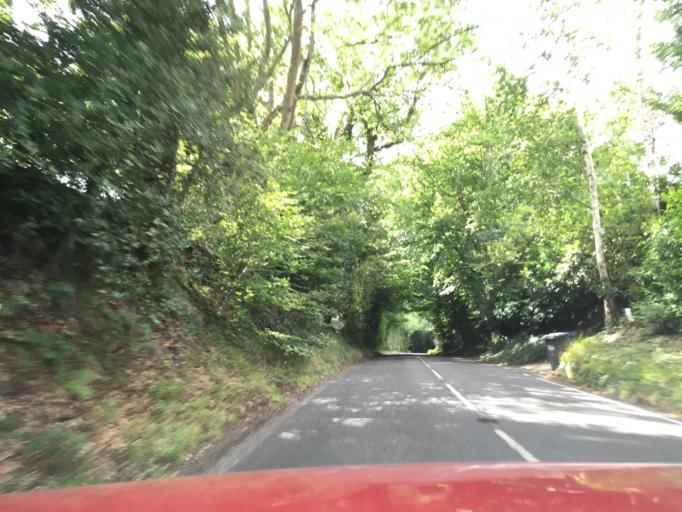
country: GB
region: England
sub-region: West Sussex
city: East Grinstead
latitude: 51.1360
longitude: 0.0153
